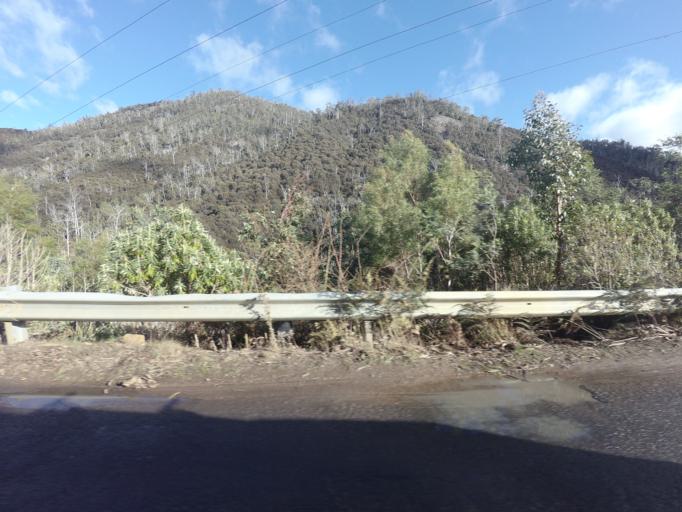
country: AU
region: Tasmania
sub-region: Glenorchy
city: Berriedale
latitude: -42.8167
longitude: 147.1763
